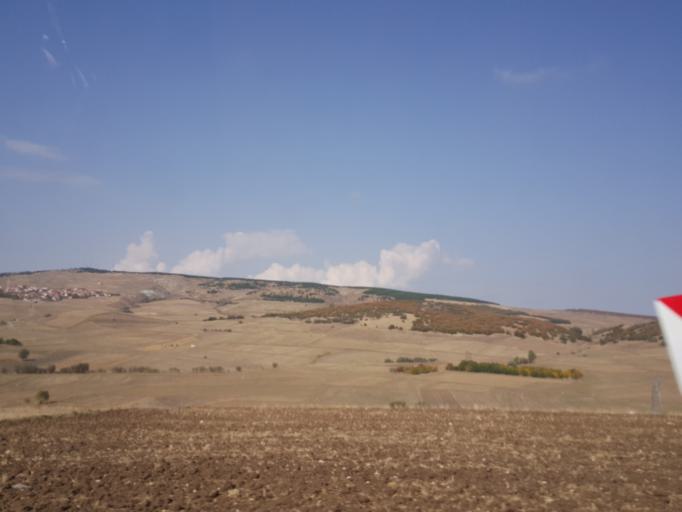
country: TR
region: Corum
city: Bogazkale
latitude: 40.1630
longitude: 34.6596
